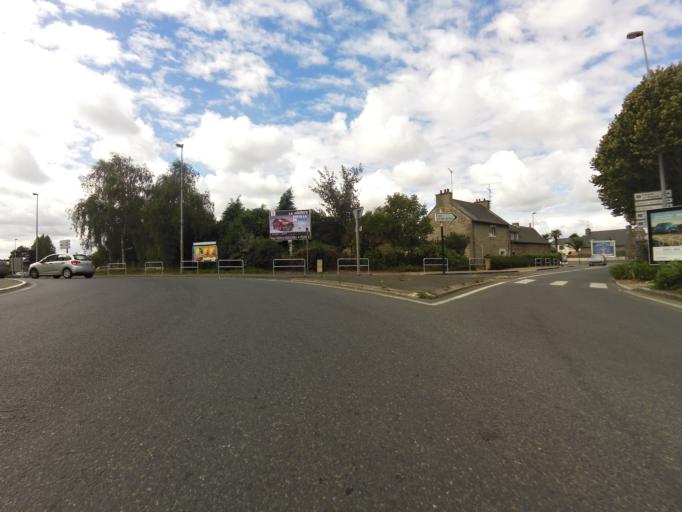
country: FR
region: Brittany
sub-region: Departement des Cotes-d'Armor
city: Saint-Brieuc
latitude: 48.4974
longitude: -2.7475
